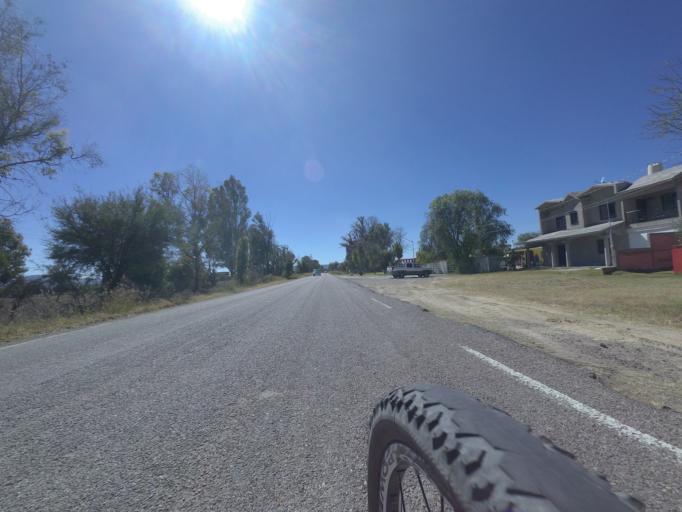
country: MX
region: Aguascalientes
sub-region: Aguascalientes
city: Los Canos
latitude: 21.8847
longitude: -102.4930
